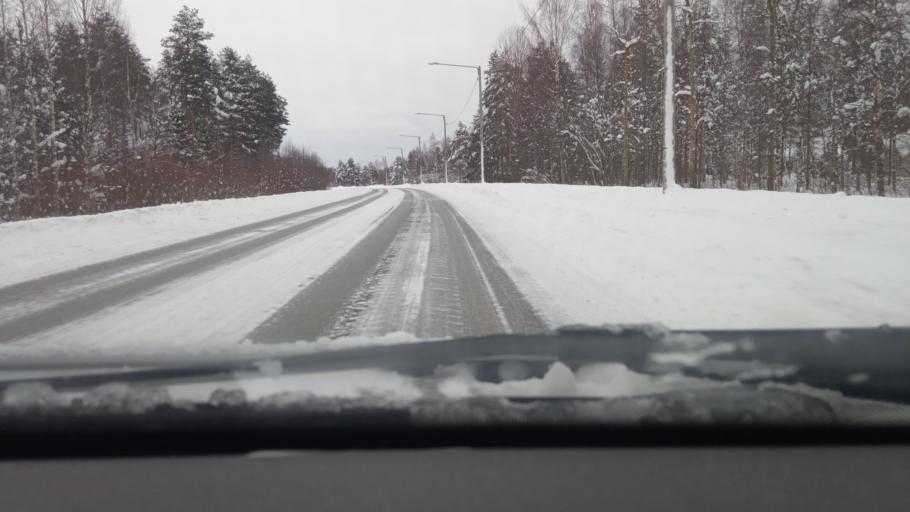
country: FI
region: Southern Ostrobothnia
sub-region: Jaerviseutu
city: Alajaervi
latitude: 62.9939
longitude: 23.8243
